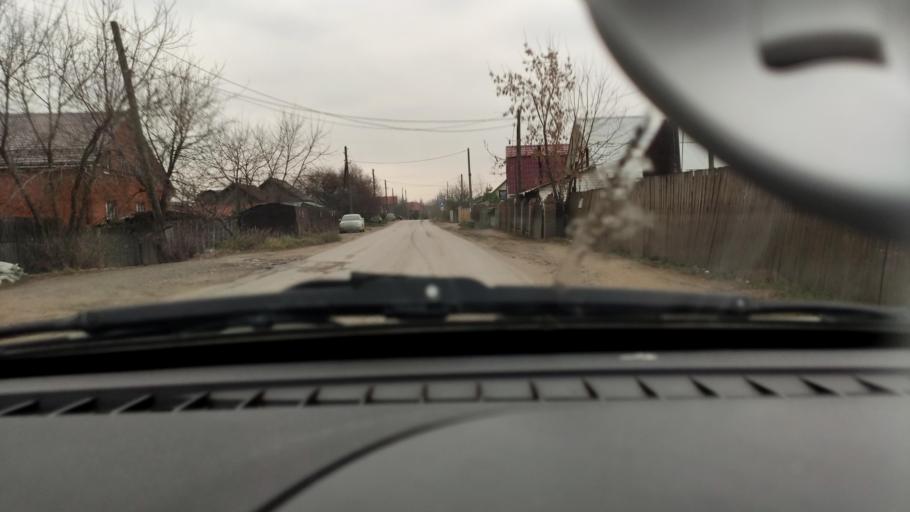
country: RU
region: Perm
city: Kondratovo
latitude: 57.9872
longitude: 56.0989
